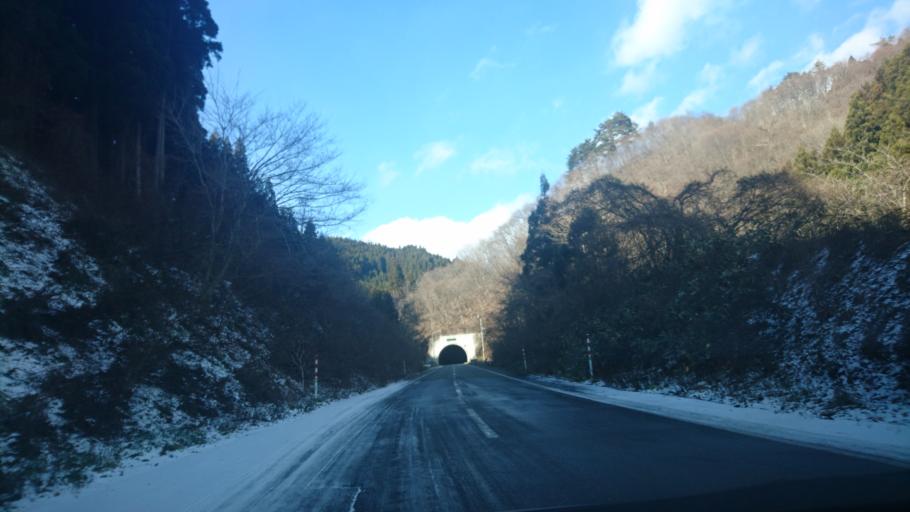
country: JP
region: Iwate
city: Mizusawa
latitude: 39.0862
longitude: 141.3873
